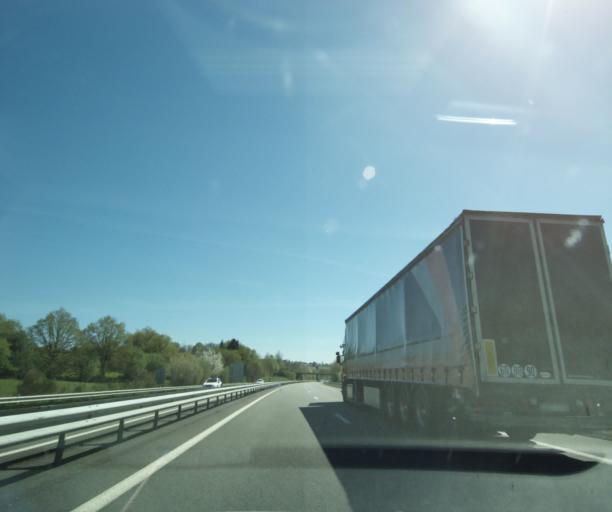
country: FR
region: Limousin
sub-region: Departement de la Haute-Vienne
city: Saint-Germain-les-Belles
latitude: 45.5571
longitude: 1.5041
